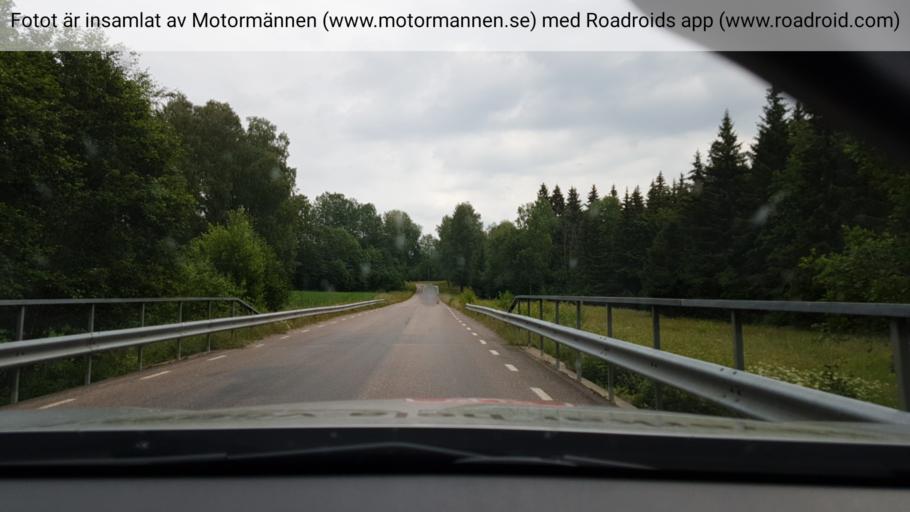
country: SE
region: Vaestra Goetaland
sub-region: Tidaholms Kommun
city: Tidaholm
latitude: 58.0702
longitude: 13.9323
